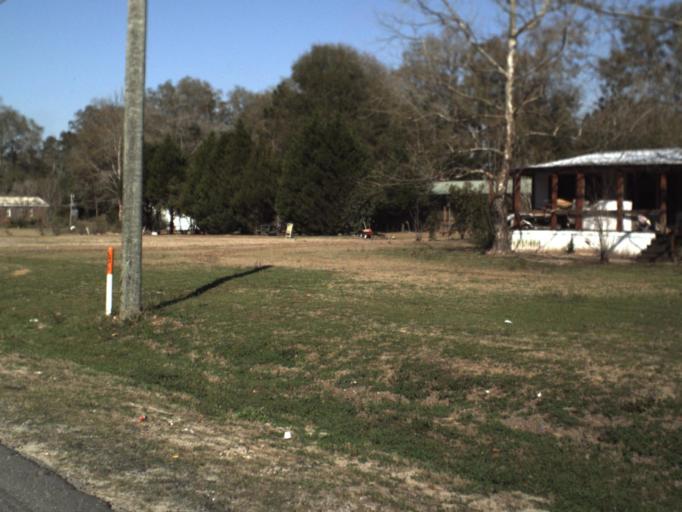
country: US
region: Florida
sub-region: Jackson County
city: Marianna
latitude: 30.7079
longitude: -85.1852
